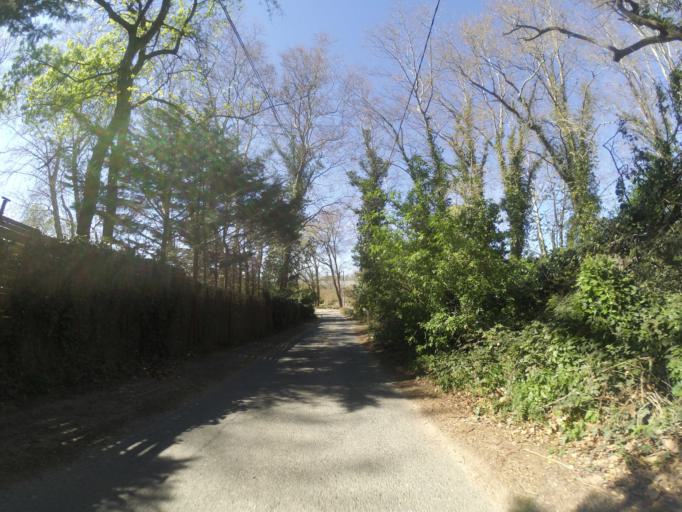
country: FR
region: Languedoc-Roussillon
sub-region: Departement des Pyrenees-Orientales
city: Toulouges
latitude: 42.6738
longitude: 2.8187
